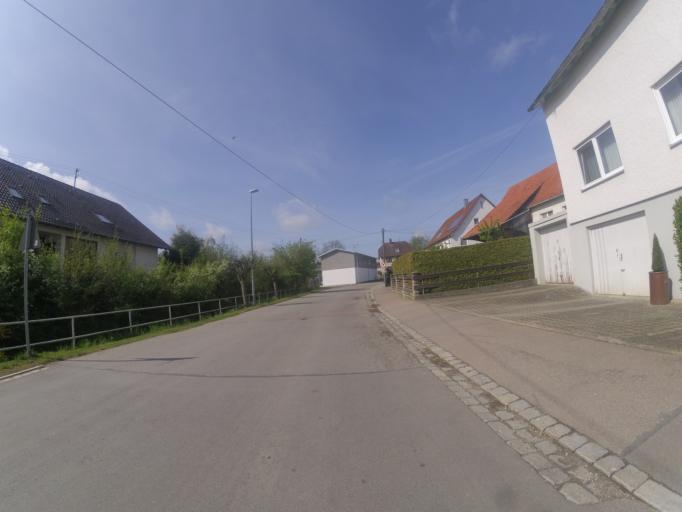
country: DE
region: Baden-Wuerttemberg
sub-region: Tuebingen Region
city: Laupheim
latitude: 48.2290
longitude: 9.8238
